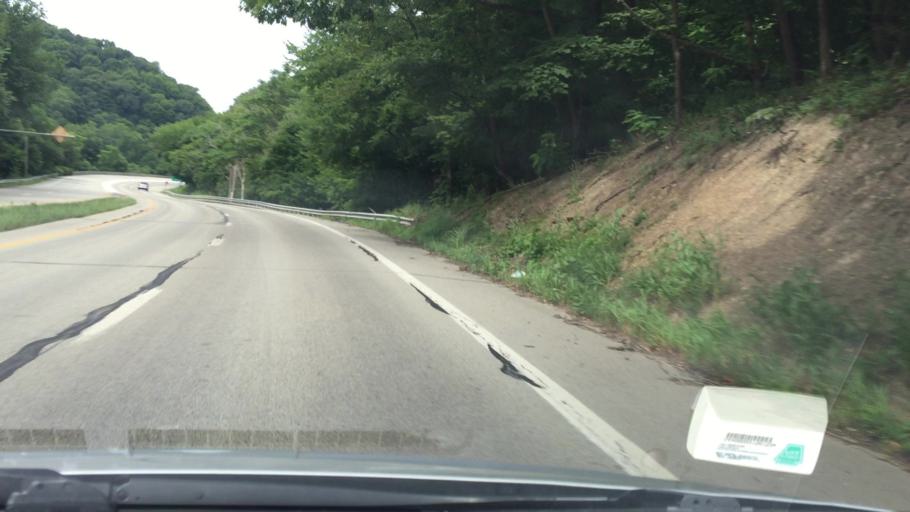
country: US
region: Pennsylvania
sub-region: Westmoreland County
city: New Kensington
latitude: 40.5764
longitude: -79.7408
